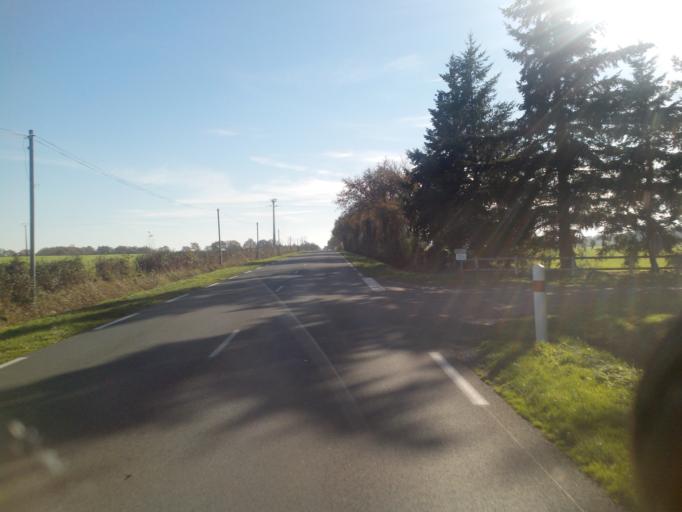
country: FR
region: Poitou-Charentes
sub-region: Departement de la Vienne
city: Saulge
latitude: 46.3172
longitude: 0.8239
